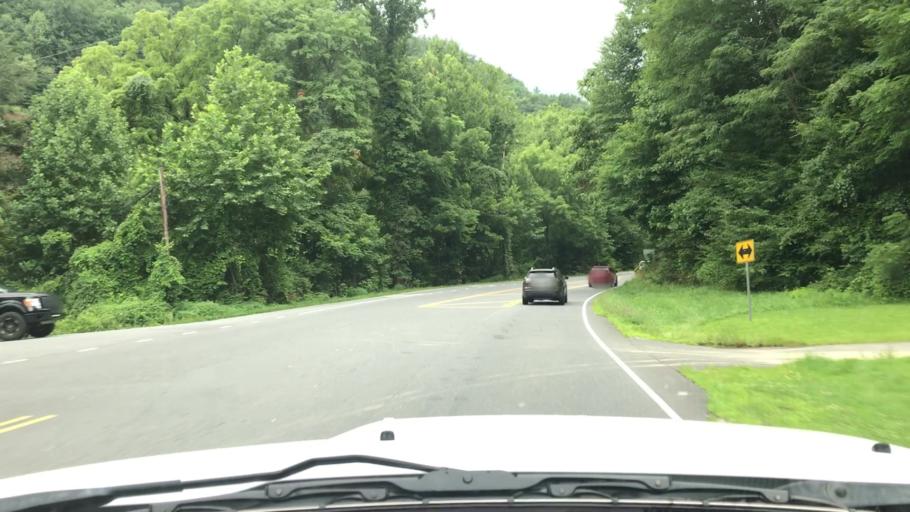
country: US
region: North Carolina
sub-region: Graham County
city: Robbinsville
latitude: 35.2738
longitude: -83.6823
